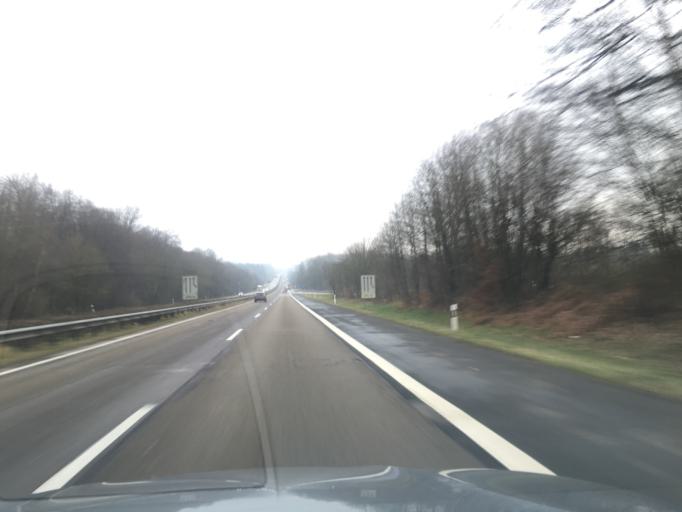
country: DE
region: Rheinland-Pfalz
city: Ebernhahn
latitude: 50.4589
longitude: 7.7619
